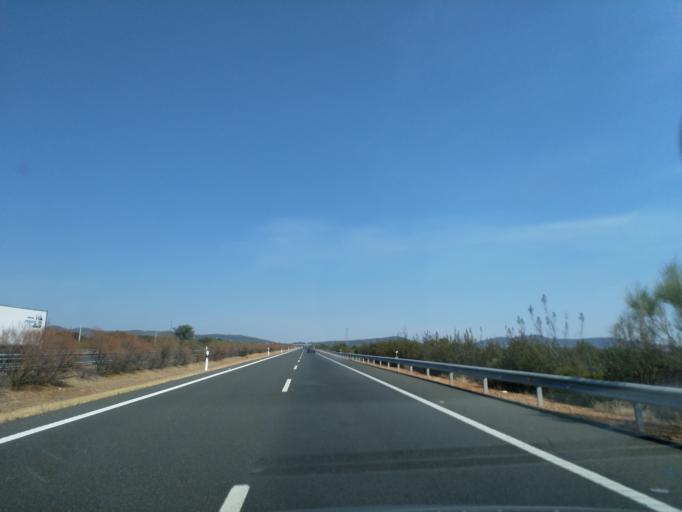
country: ES
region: Extremadura
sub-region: Provincia de Badajoz
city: Carmonita
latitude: 39.1112
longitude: -6.2805
